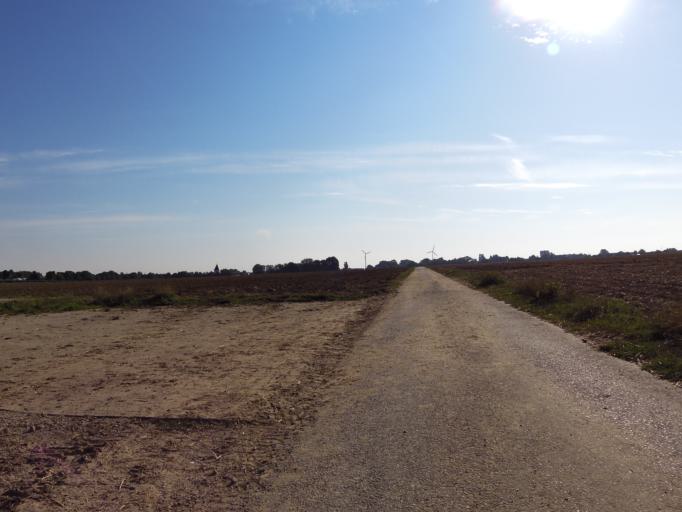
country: DE
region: North Rhine-Westphalia
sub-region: Regierungsbezirk Koln
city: Alsdorf
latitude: 50.8409
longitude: 6.1658
